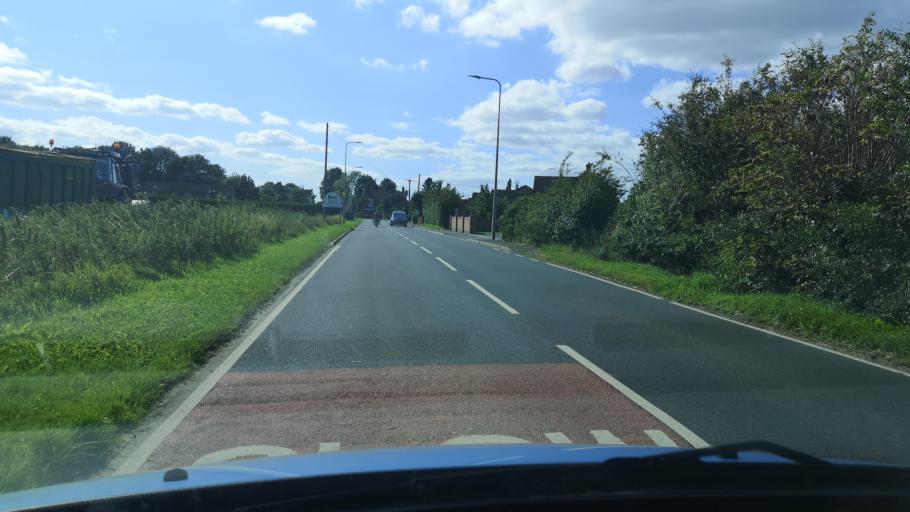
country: GB
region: England
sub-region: North Lincolnshire
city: Crowle
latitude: 53.6131
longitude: -0.8270
